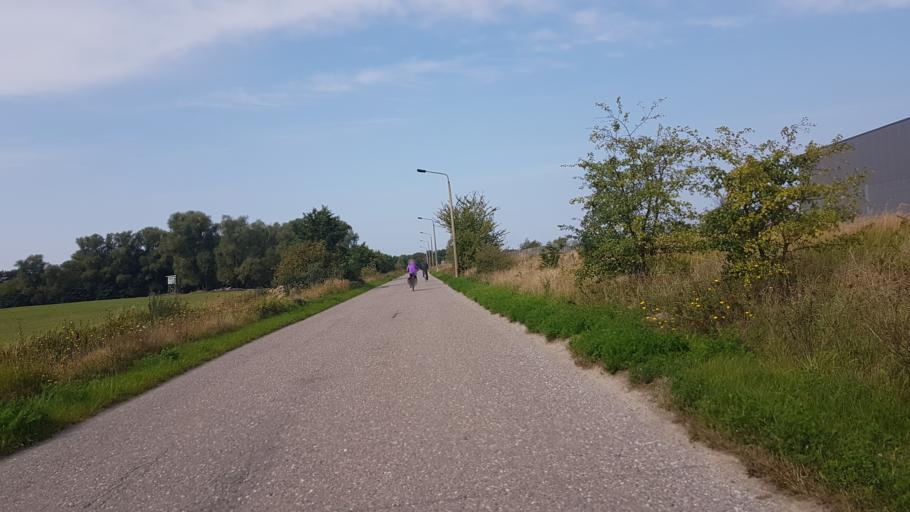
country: DE
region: Mecklenburg-Vorpommern
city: Sagard
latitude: 54.4937
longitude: 13.5598
